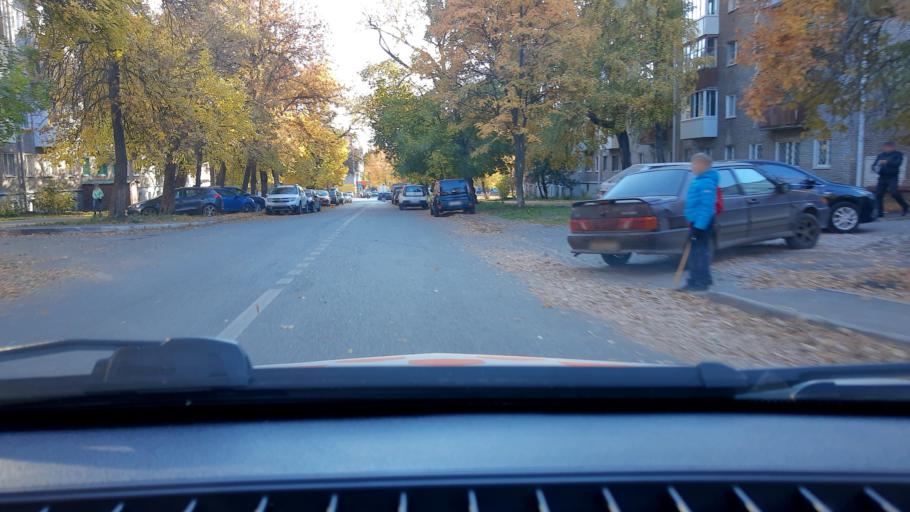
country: RU
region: Bashkortostan
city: Ufa
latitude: 54.8087
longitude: 56.1113
